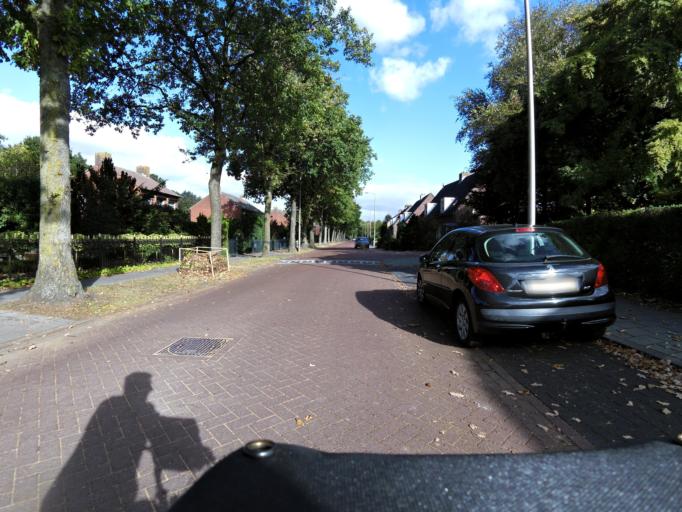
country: NL
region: North Brabant
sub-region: Gemeente Bergen op Zoom
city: Lepelstraat
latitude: 51.5500
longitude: 4.2731
